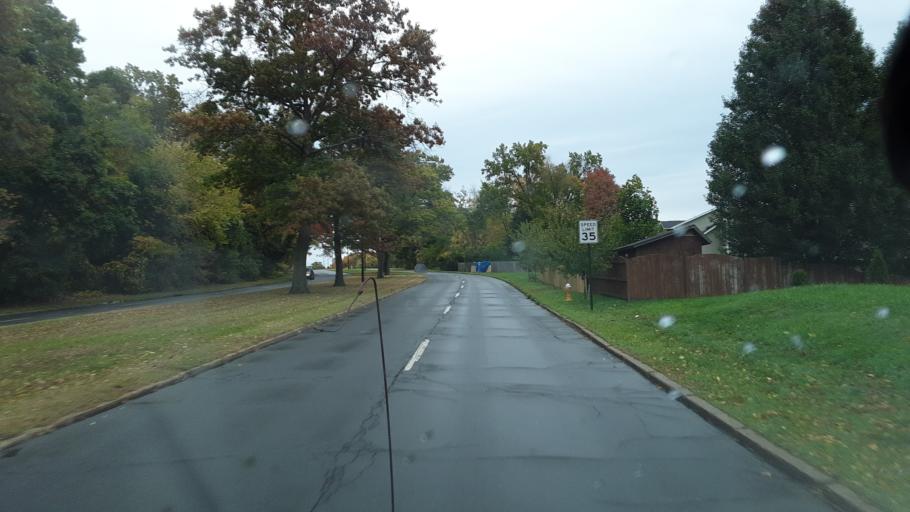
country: US
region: Ohio
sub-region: Summit County
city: Sawyerwood
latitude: 41.0328
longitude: -81.4603
